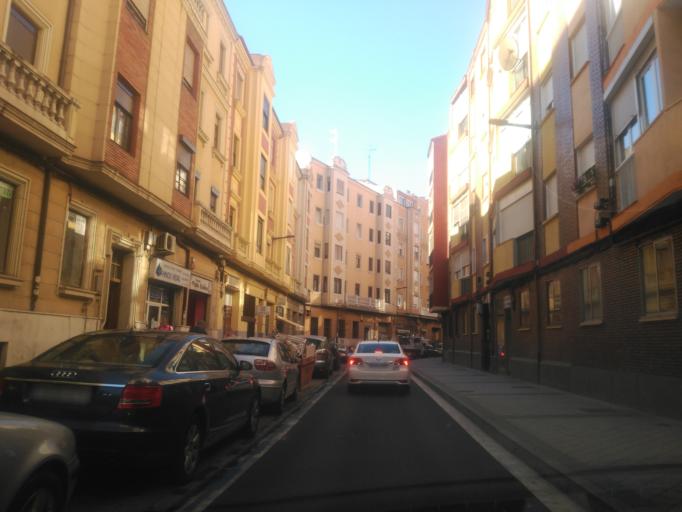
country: ES
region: Castille and Leon
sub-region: Provincia de Valladolid
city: Valladolid
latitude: 41.6469
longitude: -4.7179
